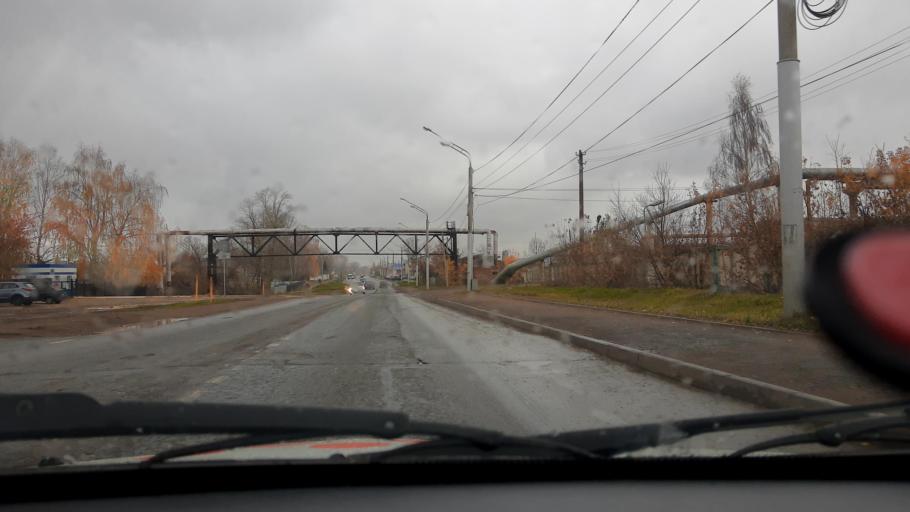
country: RU
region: Bashkortostan
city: Iglino
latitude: 54.7633
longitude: 56.2396
